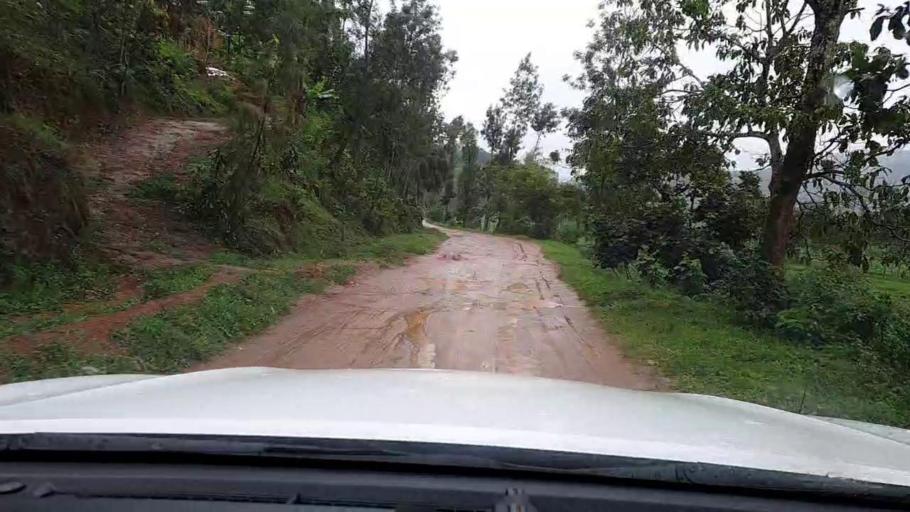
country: RW
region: Northern Province
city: Byumba
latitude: -1.7262
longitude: 29.9339
